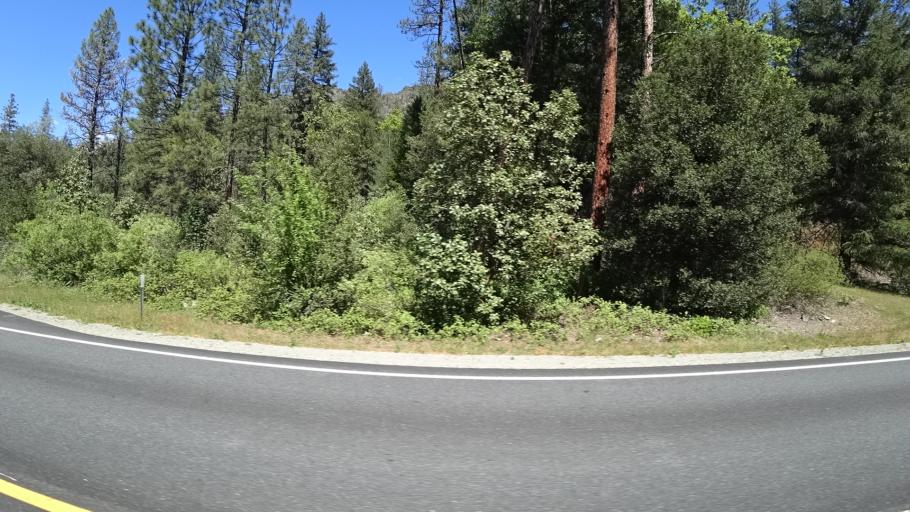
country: US
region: California
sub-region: Trinity County
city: Weaverville
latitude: 40.7399
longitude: -123.0615
